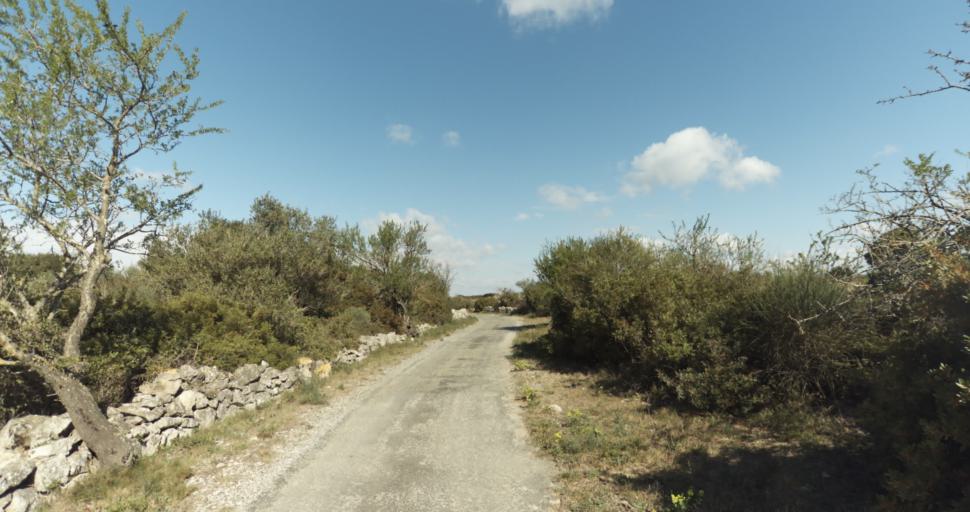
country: FR
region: Languedoc-Roussillon
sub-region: Departement de l'Aude
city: Leucate
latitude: 42.9185
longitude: 3.0310
